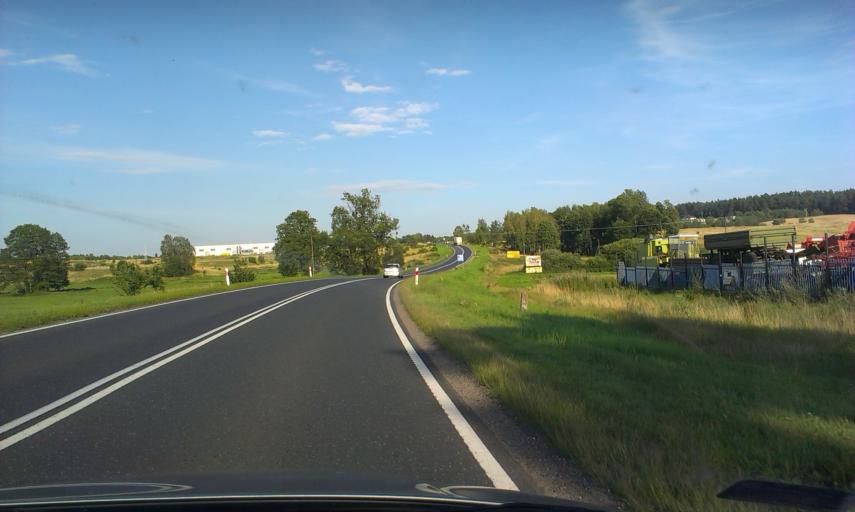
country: PL
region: Kujawsko-Pomorskie
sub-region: Powiat bydgoski
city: Sicienko
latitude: 53.1608
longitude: 17.8173
